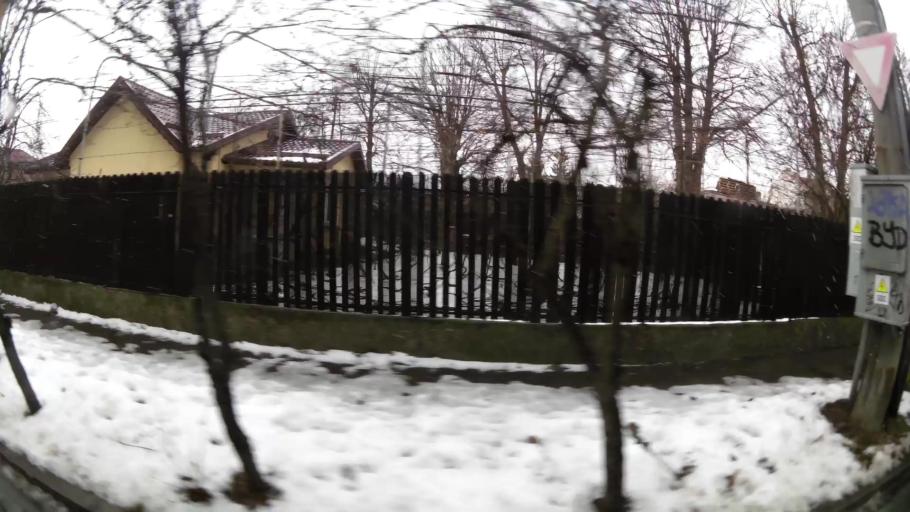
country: RO
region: Ilfov
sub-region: Comuna Chiajna
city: Rosu
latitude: 44.4913
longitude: 26.0438
